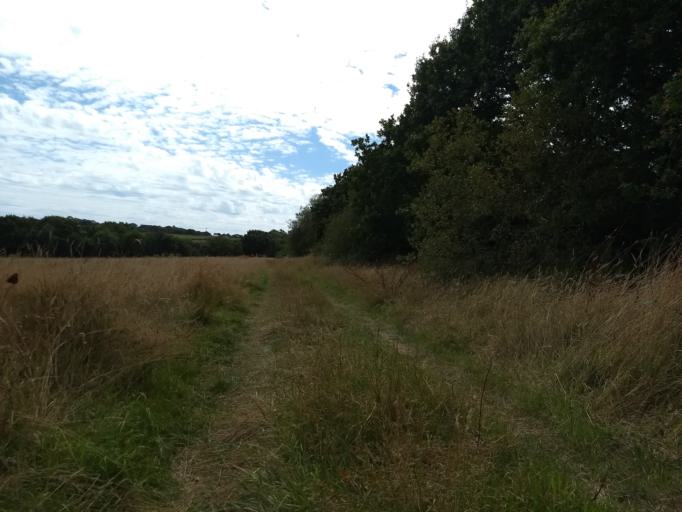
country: GB
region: England
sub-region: Isle of Wight
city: Newport
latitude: 50.7123
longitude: -1.2688
